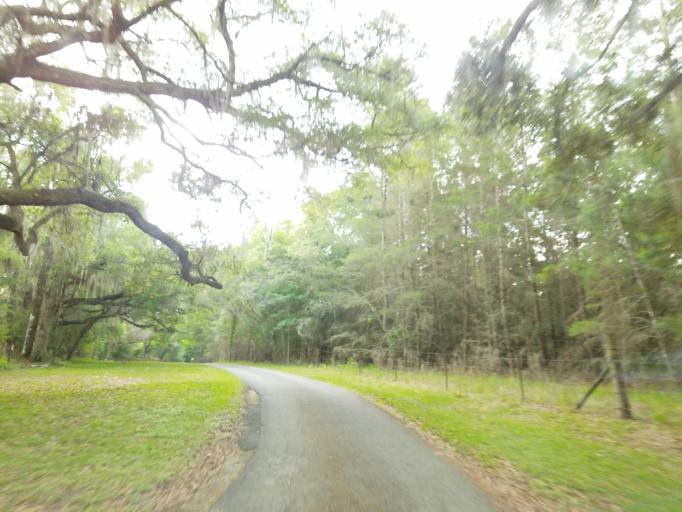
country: US
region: Florida
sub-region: Hernando County
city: Brooksville
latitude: 28.6131
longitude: -82.3510
